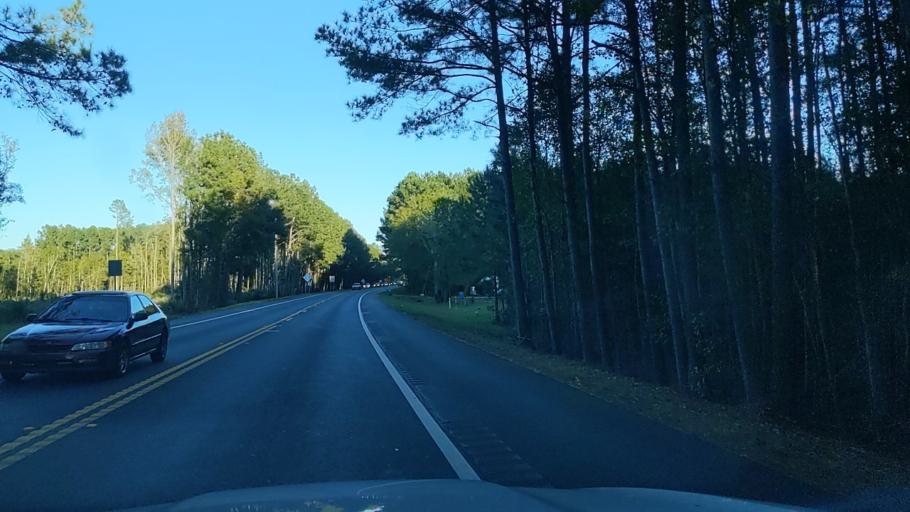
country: US
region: Georgia
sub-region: Chatham County
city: Port Wentworth
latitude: 32.1951
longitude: -81.2161
